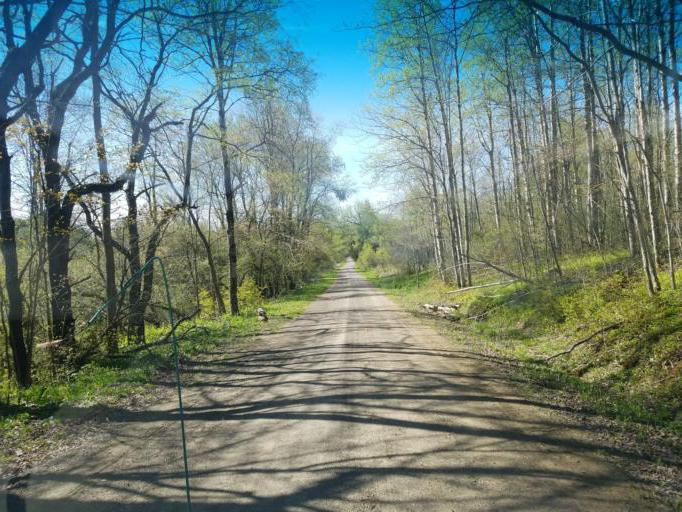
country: US
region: New York
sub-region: Allegany County
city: Andover
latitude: 41.9669
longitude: -77.7829
